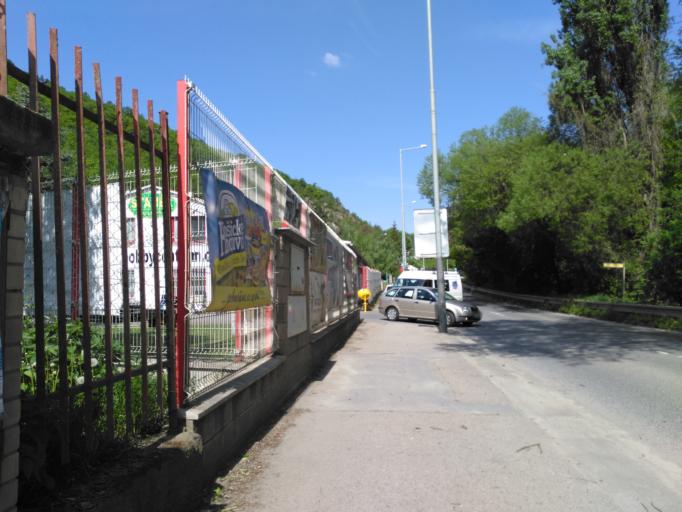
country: CZ
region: Central Bohemia
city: Cernosice
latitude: 49.9930
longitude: 14.3443
